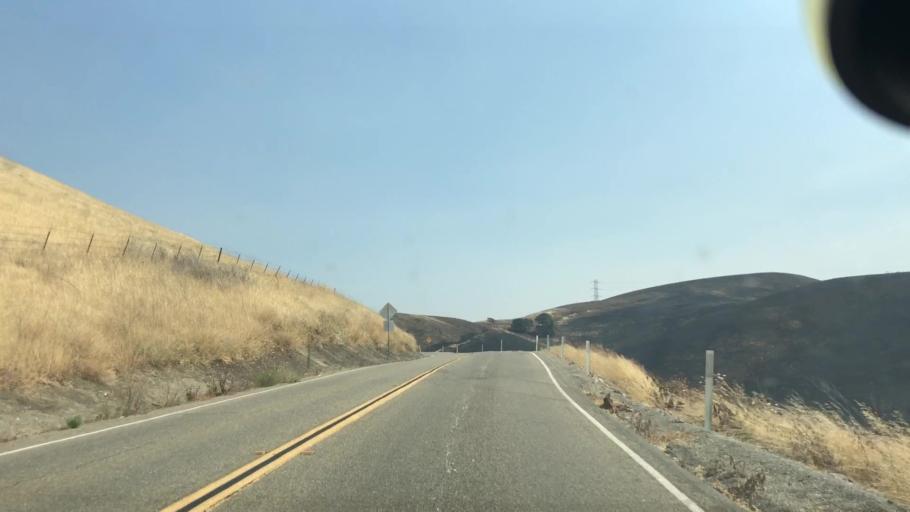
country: US
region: California
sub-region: San Joaquin County
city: Mountain House
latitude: 37.6511
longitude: -121.6133
